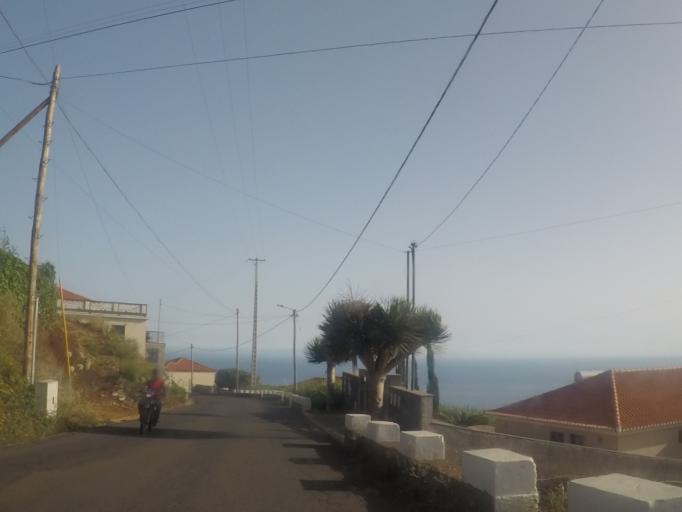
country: PT
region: Madeira
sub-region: Calheta
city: Arco da Calheta
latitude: 32.7032
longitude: -17.1258
